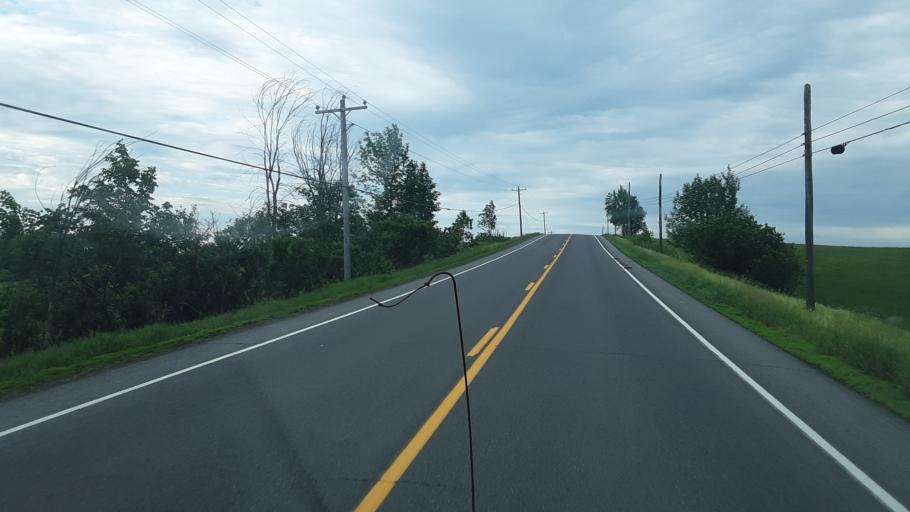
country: US
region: Maine
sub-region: Penobscot County
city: Patten
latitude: 45.9560
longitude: -68.4522
